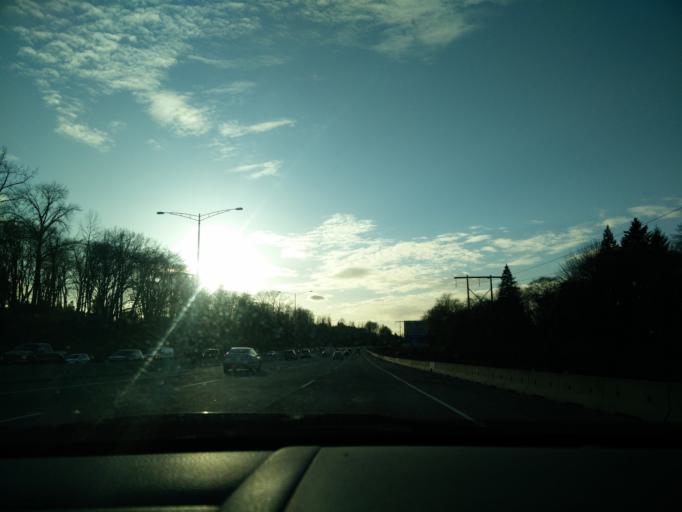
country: CA
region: British Columbia
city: Burnaby
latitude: 49.2370
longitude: -122.9385
